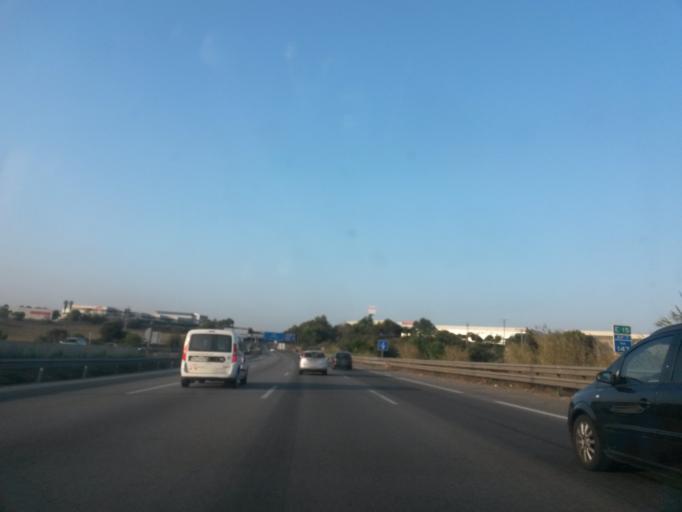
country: ES
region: Catalonia
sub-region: Provincia de Barcelona
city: Barbera del Valles
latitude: 41.5118
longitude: 2.1407
